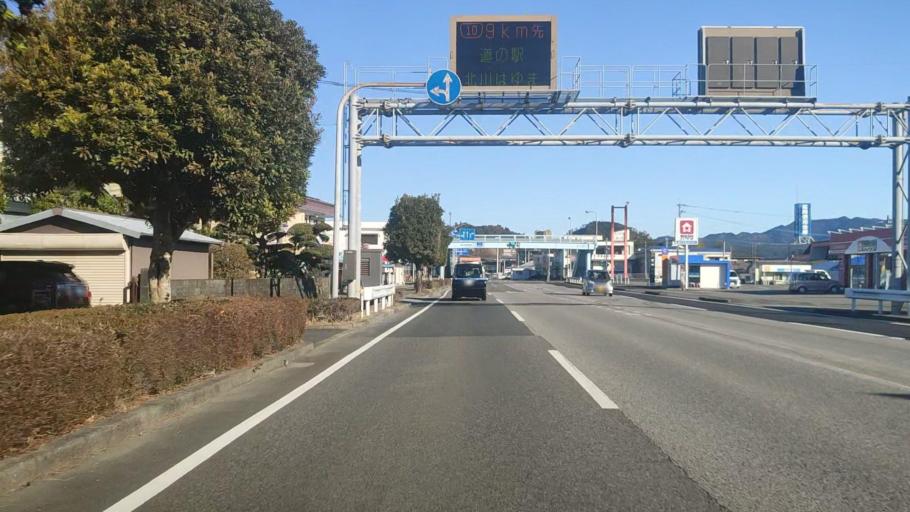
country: JP
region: Miyazaki
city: Nobeoka
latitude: 32.6000
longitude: 131.6822
